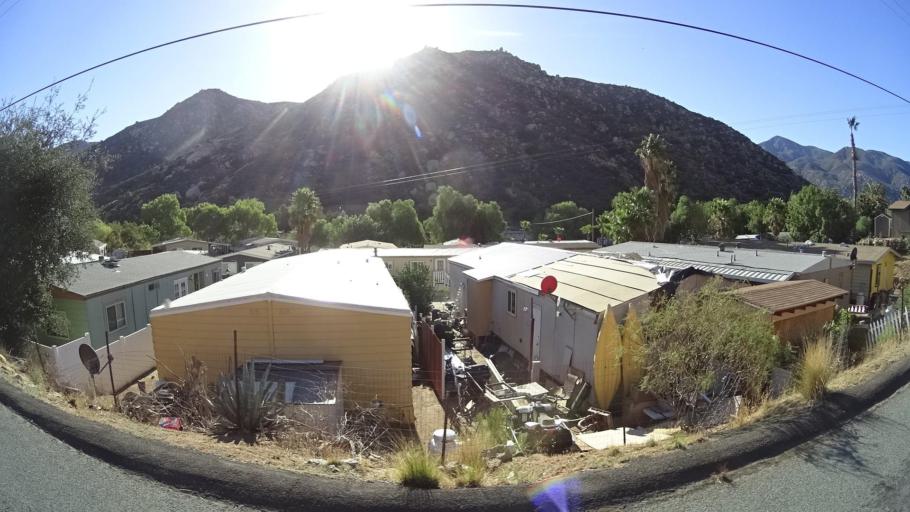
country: MX
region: Baja California
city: Tecate
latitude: 32.6232
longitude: -116.6915
